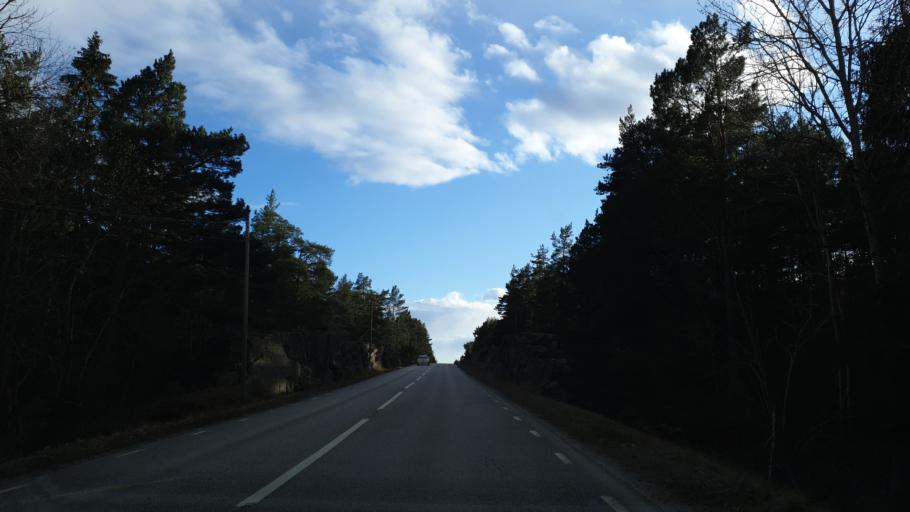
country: SE
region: Stockholm
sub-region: Varmdo Kommun
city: Holo
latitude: 59.3015
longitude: 18.6742
